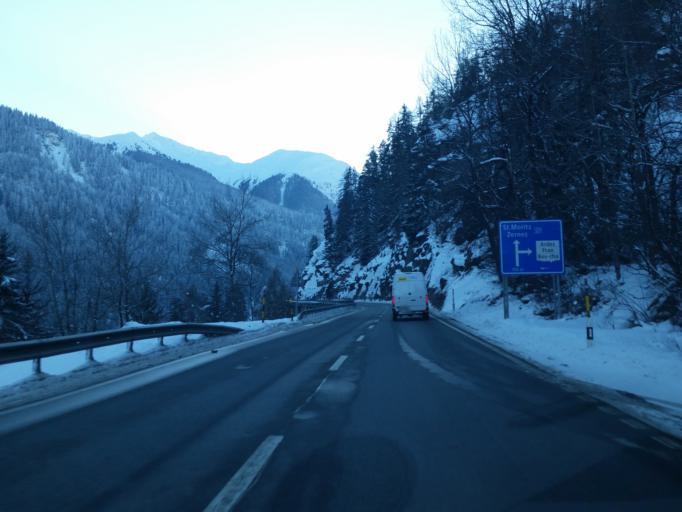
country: CH
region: Grisons
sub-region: Inn District
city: Scuol
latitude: 46.7741
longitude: 10.2177
